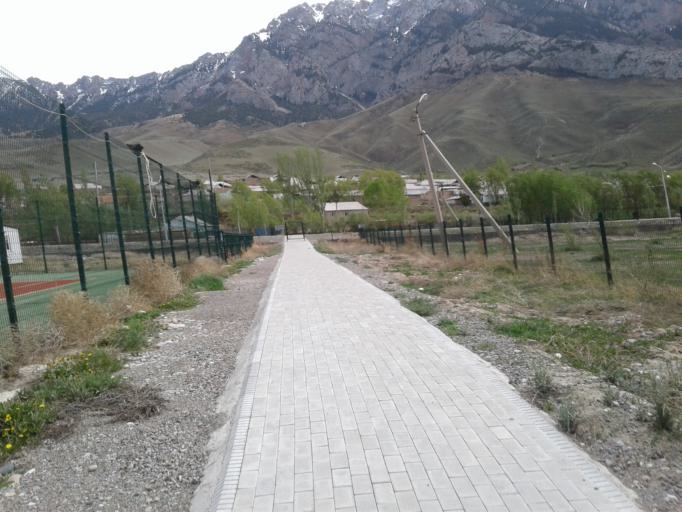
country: KG
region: Naryn
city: Naryn
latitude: 41.4317
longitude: 75.9082
